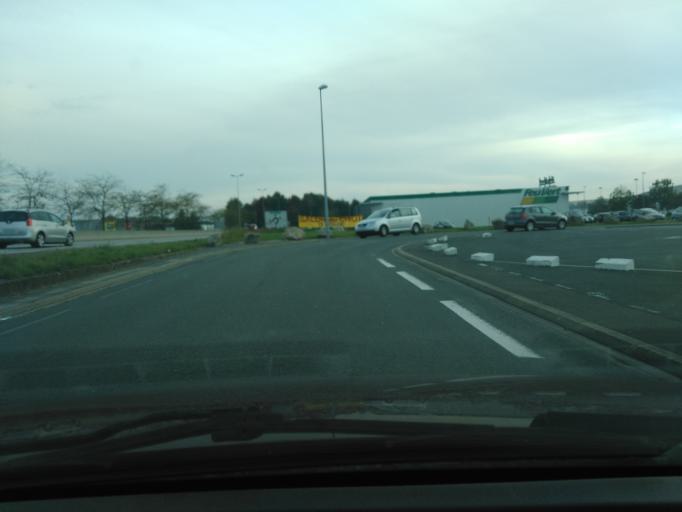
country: FR
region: Pays de la Loire
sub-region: Departement de la Vendee
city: Mouilleron-le-Captif
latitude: 46.7012
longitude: -1.4298
